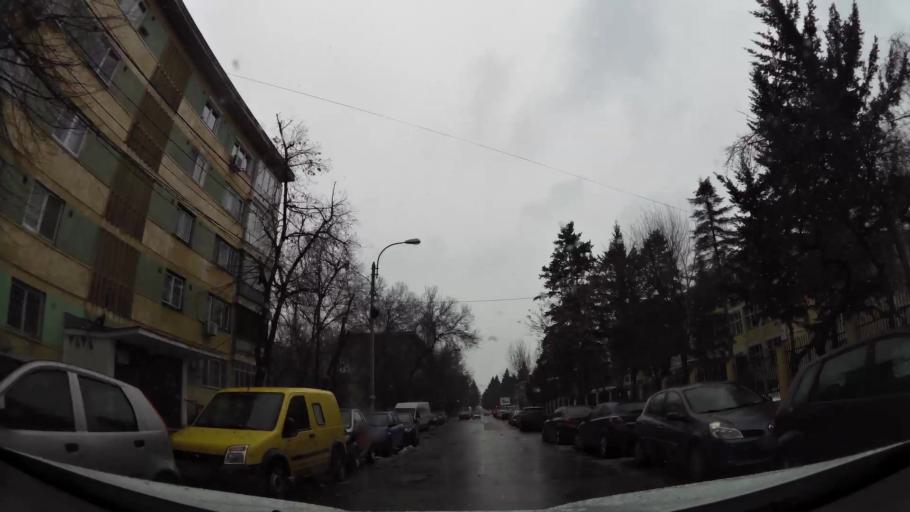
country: RO
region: Bucuresti
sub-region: Municipiul Bucuresti
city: Bucuresti
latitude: 44.4271
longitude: 26.0520
